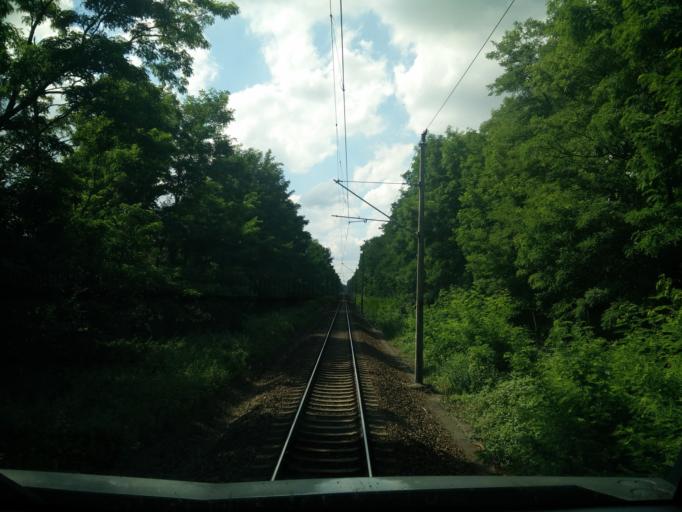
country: DE
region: Brandenburg
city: Kolkwitz
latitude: 51.7531
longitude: 14.2752
